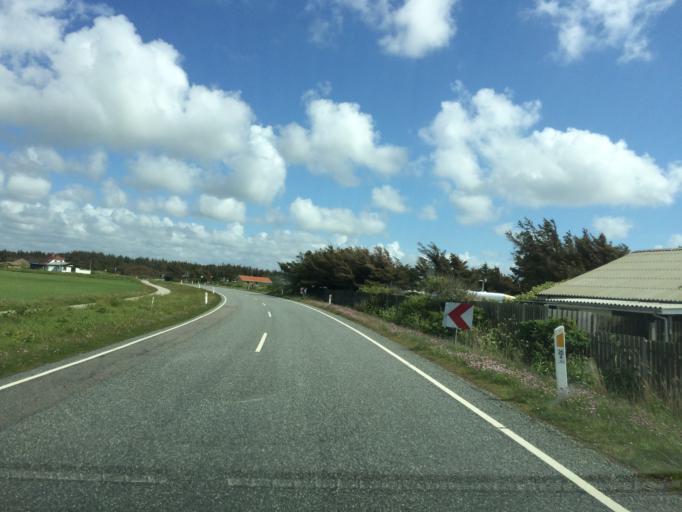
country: DK
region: Central Jutland
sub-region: Holstebro Kommune
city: Ulfborg
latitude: 56.3229
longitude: 8.1249
